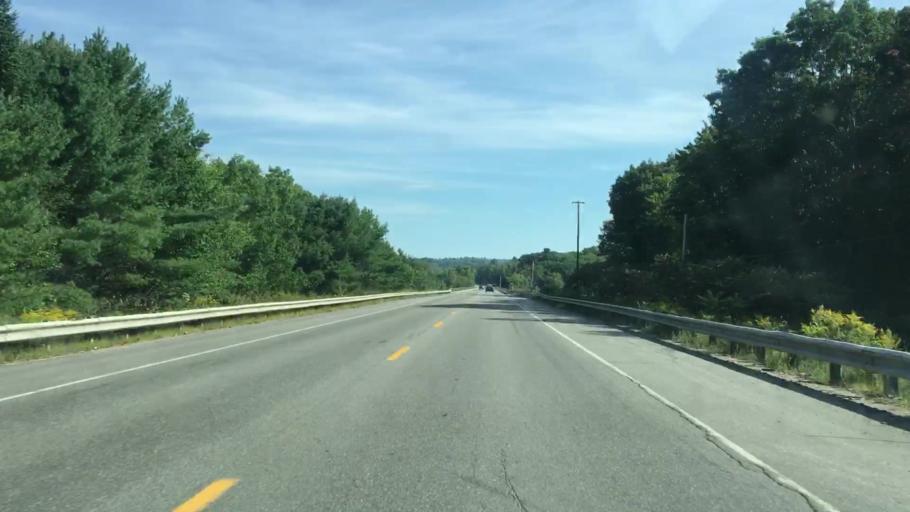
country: US
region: Maine
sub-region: Penobscot County
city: Lincoln
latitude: 45.3648
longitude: -68.5503
